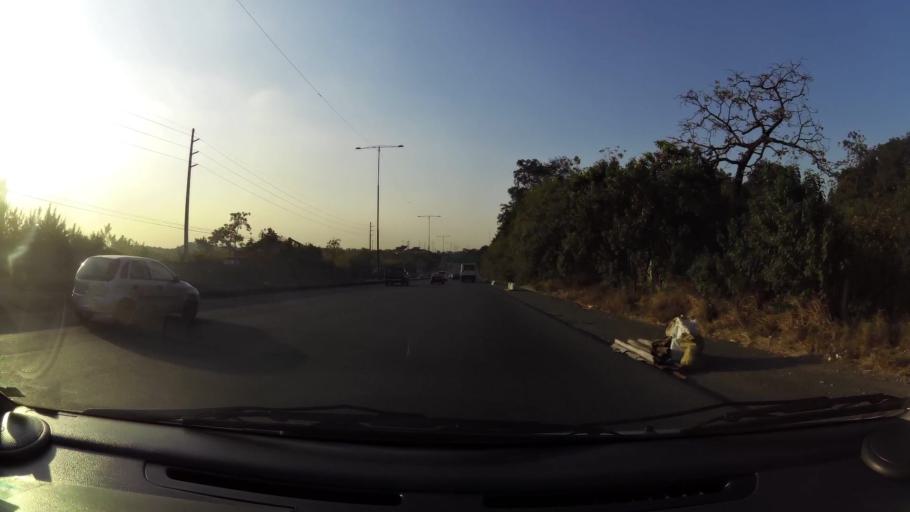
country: EC
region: Guayas
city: Santa Lucia
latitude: -2.1464
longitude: -79.9456
